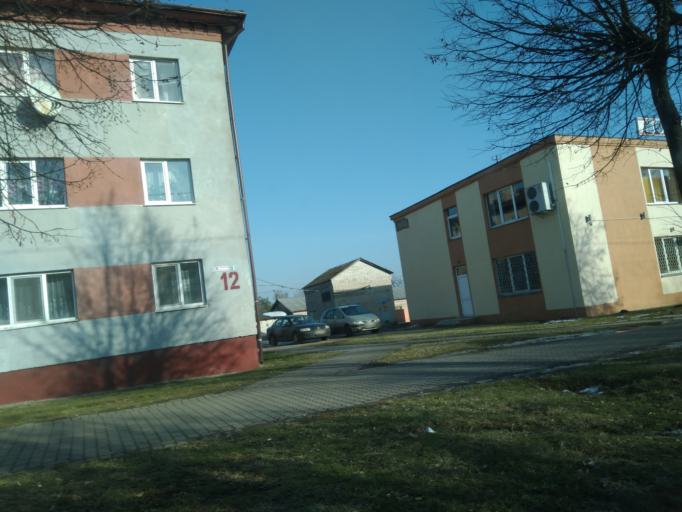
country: BY
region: Minsk
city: Snow
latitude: 53.2211
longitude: 26.4006
